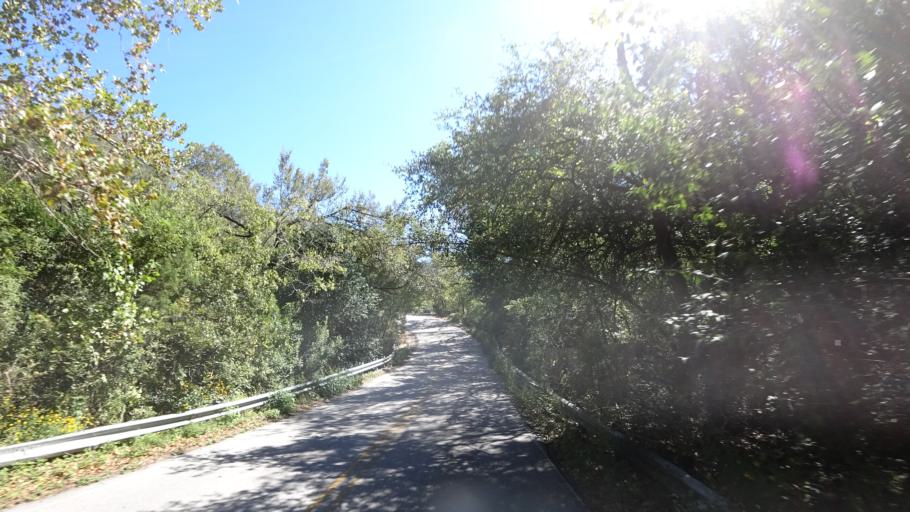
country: US
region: Texas
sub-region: Travis County
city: West Lake Hills
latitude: 30.3366
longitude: -97.7768
